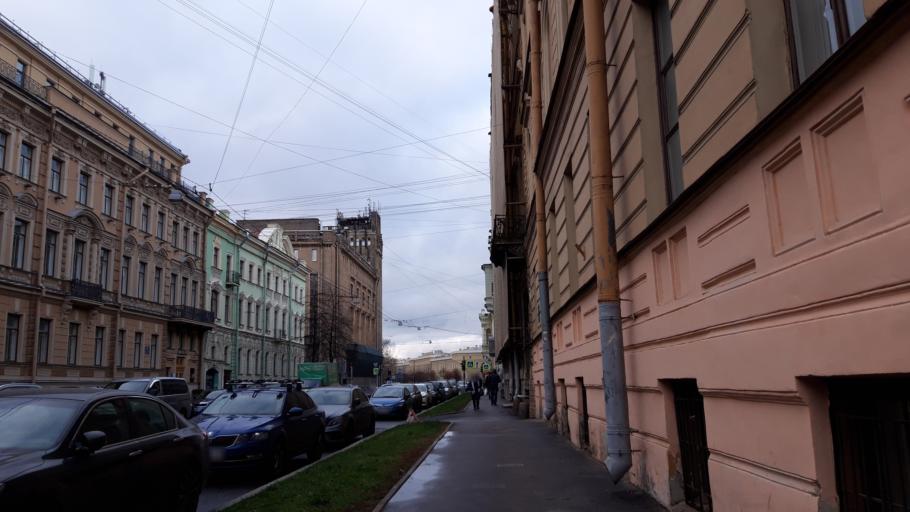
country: RU
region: St.-Petersburg
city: Saint Petersburg
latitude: 59.9317
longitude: 30.3046
